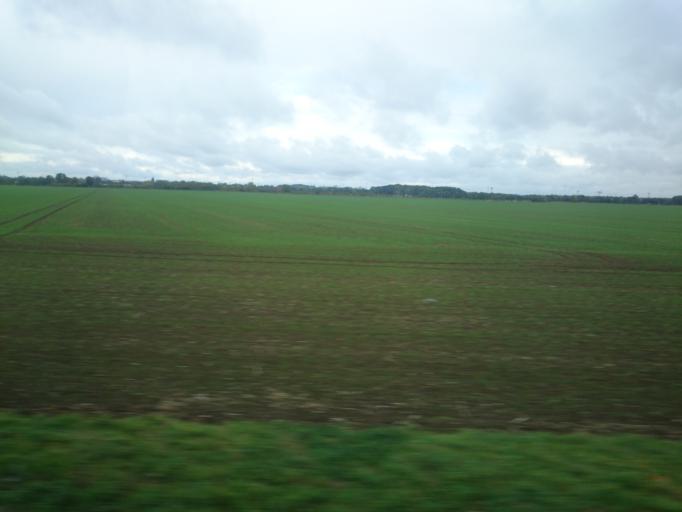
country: DE
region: Saxony-Anhalt
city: Grobers
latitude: 51.4238
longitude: 12.1272
